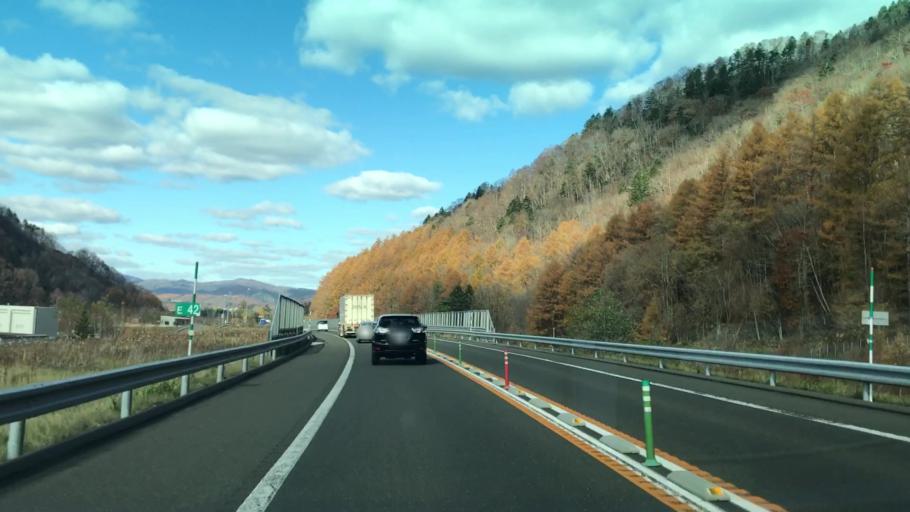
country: JP
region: Hokkaido
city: Iwamizawa
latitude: 42.9216
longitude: 142.0366
